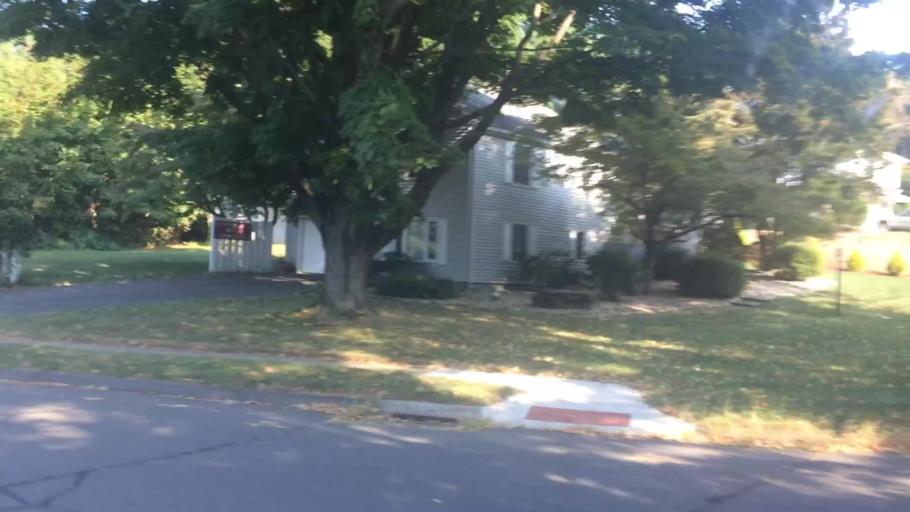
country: US
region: Connecticut
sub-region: Hartford County
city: Kensington
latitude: 41.6088
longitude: -72.7541
